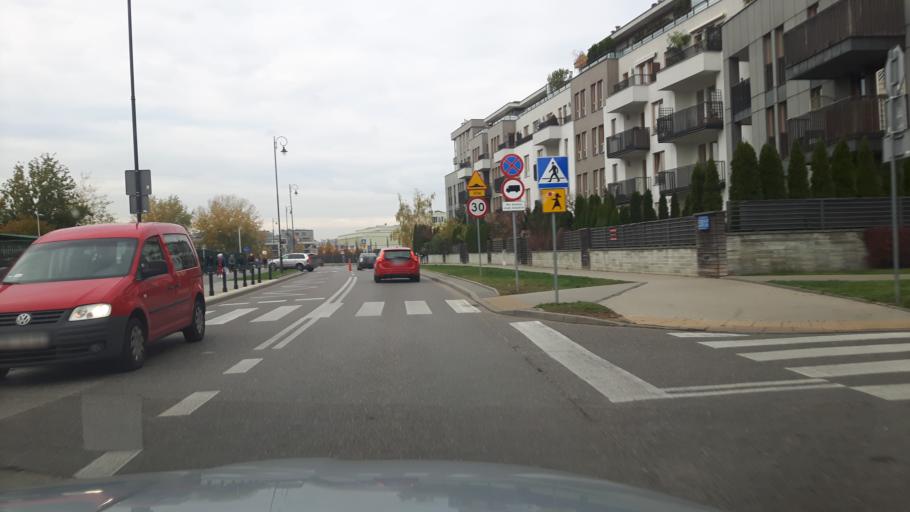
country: PL
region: Masovian Voivodeship
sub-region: Warszawa
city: Wilanow
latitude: 52.1557
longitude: 21.0704
